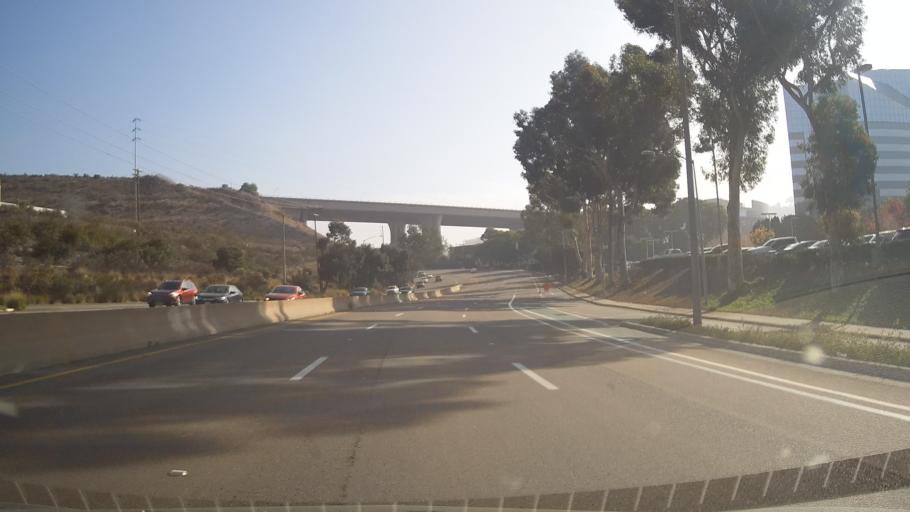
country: US
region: California
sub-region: San Diego County
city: San Diego
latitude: 32.7781
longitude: -117.1410
